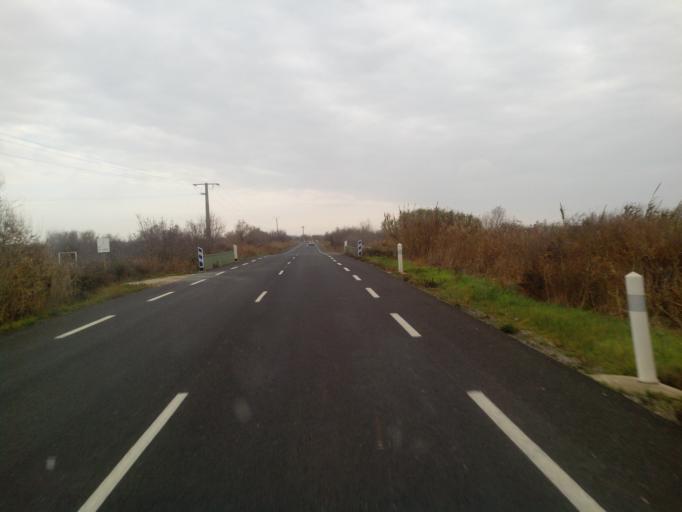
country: FR
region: Languedoc-Roussillon
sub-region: Departement du Gard
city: Aigues-Mortes
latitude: 43.5587
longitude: 4.3186
